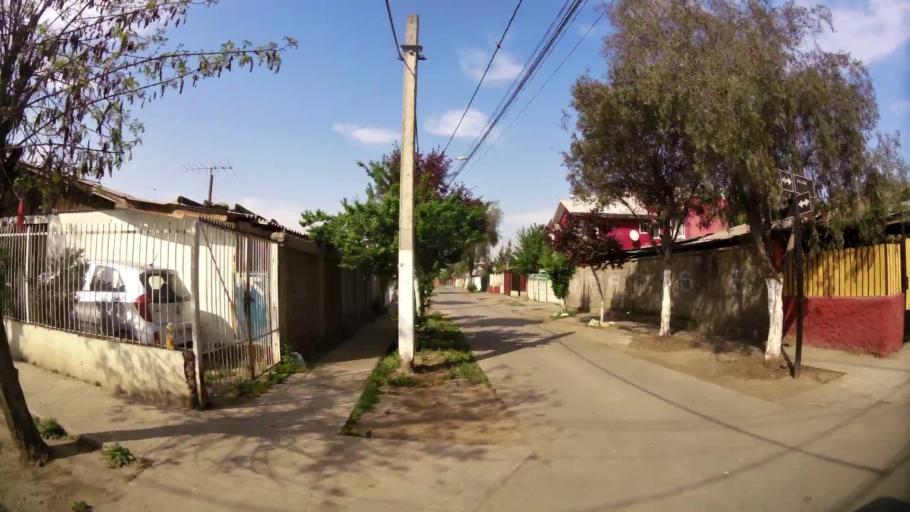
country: CL
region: Santiago Metropolitan
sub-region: Provincia de Santiago
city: Lo Prado
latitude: -33.4491
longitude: -70.7435
